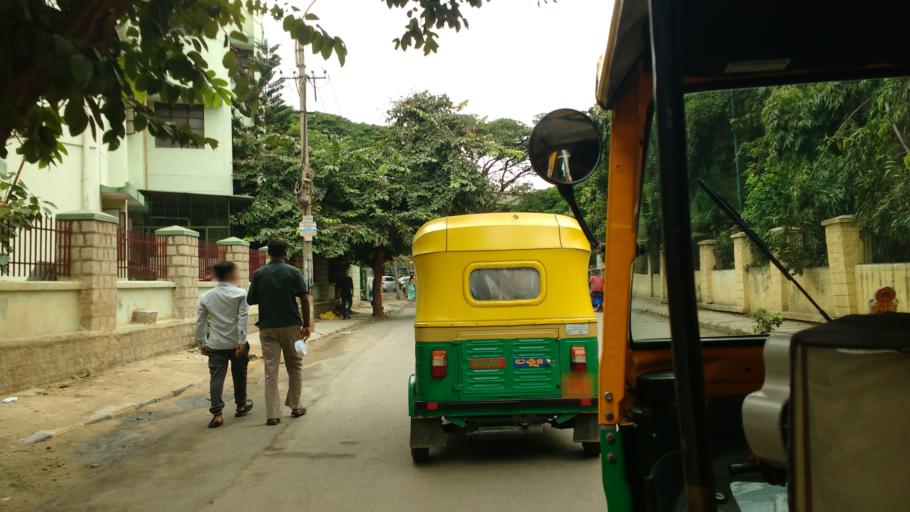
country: IN
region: Karnataka
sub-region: Bangalore Urban
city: Bangalore
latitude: 12.9736
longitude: 77.5385
